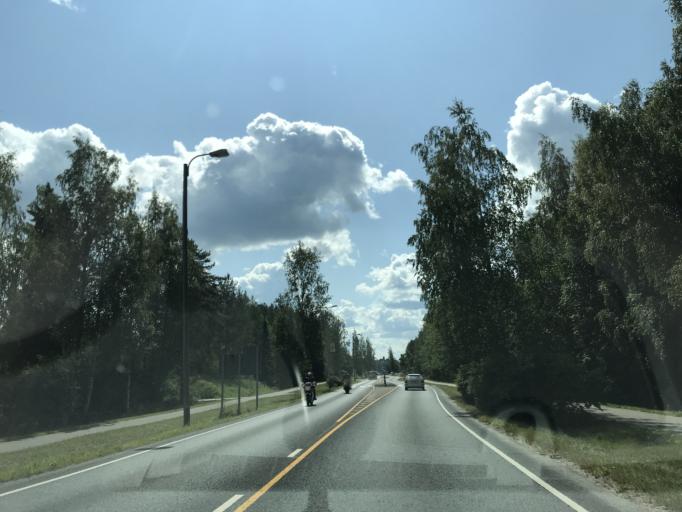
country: FI
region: Paijanne Tavastia
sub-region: Lahti
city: Orimattila
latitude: 60.8178
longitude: 25.7303
